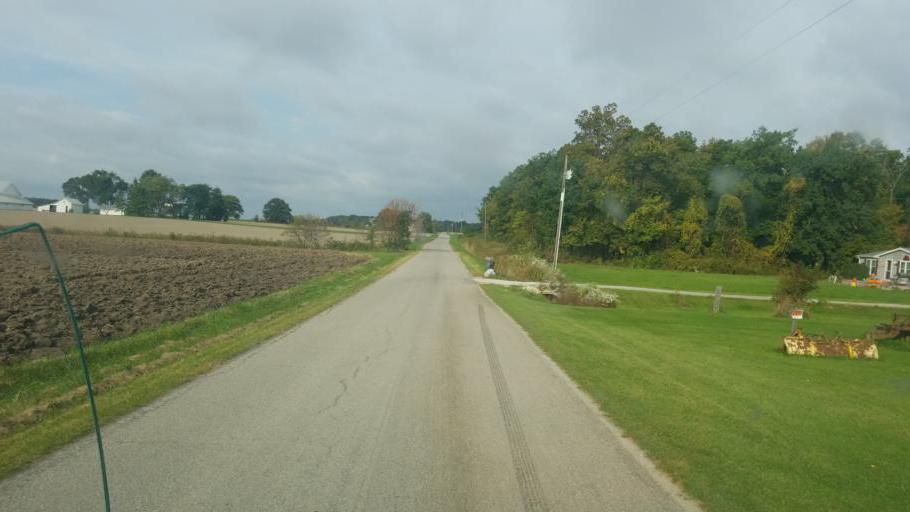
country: US
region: Ohio
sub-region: Seneca County
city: Fostoria
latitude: 41.0501
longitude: -83.4857
